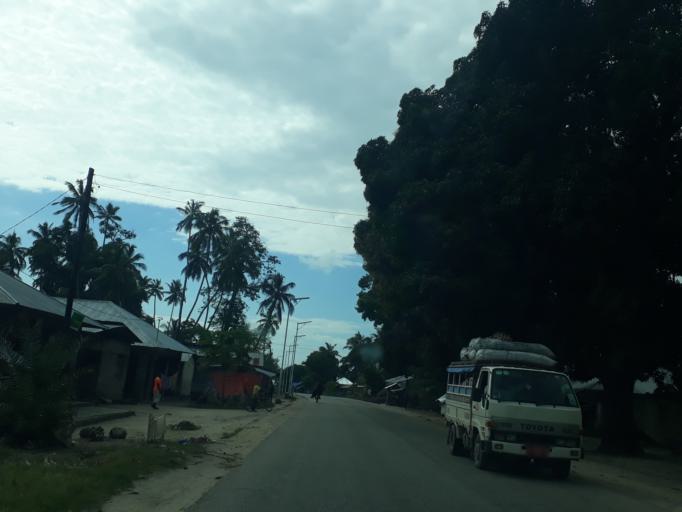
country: TZ
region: Zanzibar North
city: Mkokotoni
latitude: -5.8780
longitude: 39.2556
